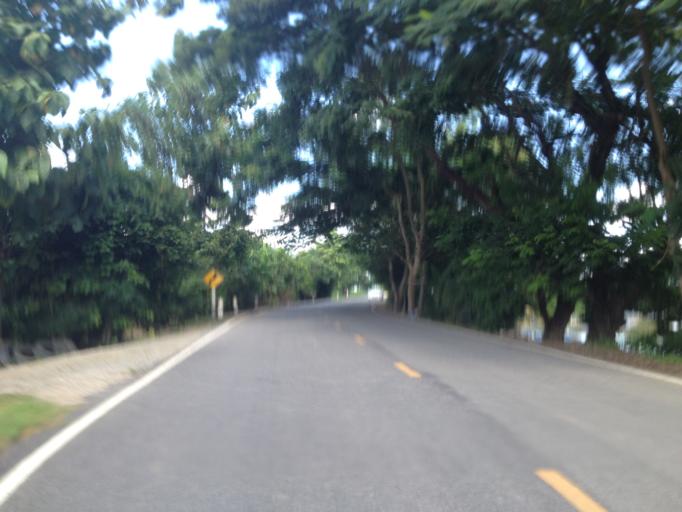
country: TH
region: Chiang Mai
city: Hang Dong
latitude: 18.6530
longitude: 98.9585
